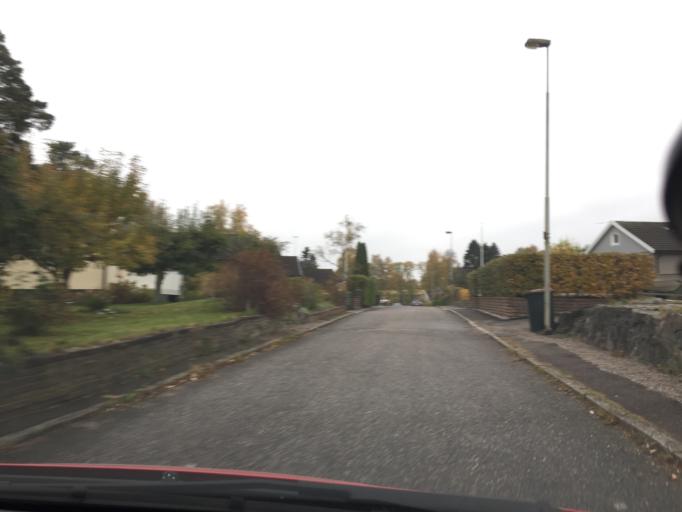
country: SE
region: Vaestra Goetaland
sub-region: Trollhattan
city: Trollhattan
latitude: 58.2825
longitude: 12.3148
